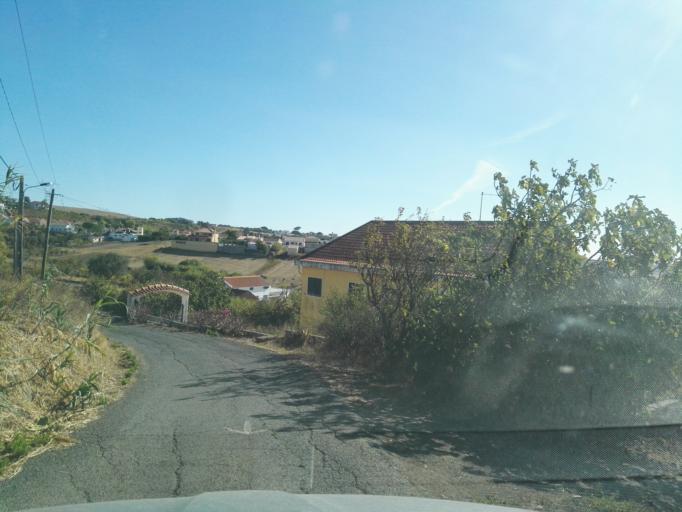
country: PT
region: Lisbon
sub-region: Vila Franca de Xira
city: Sao Joao dos Montes
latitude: 38.9588
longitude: -9.0464
